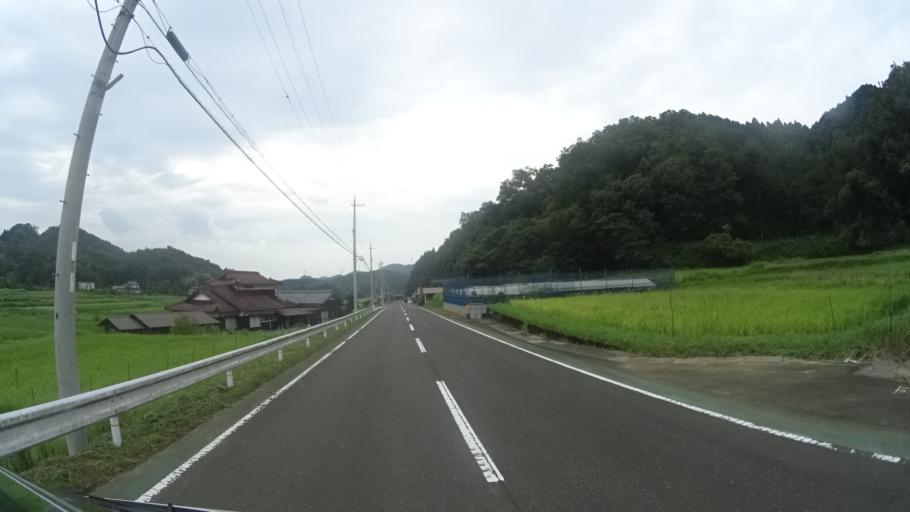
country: JP
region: Kyoto
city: Maizuru
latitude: 35.3564
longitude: 135.3267
